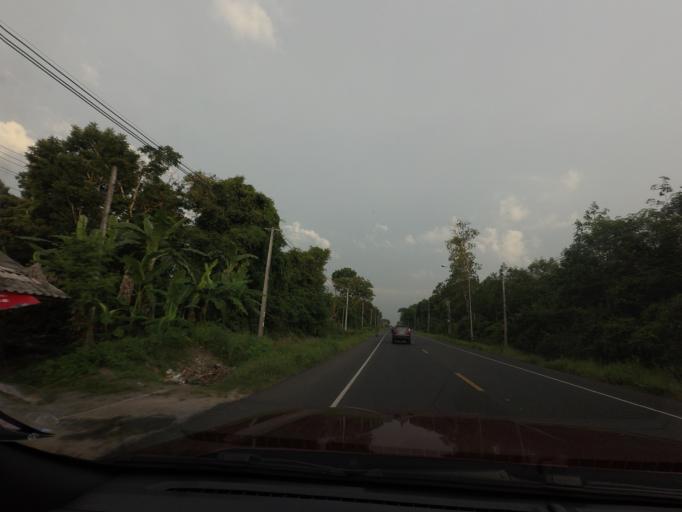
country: TH
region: Pattani
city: Mae Lan
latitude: 6.6091
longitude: 101.1918
